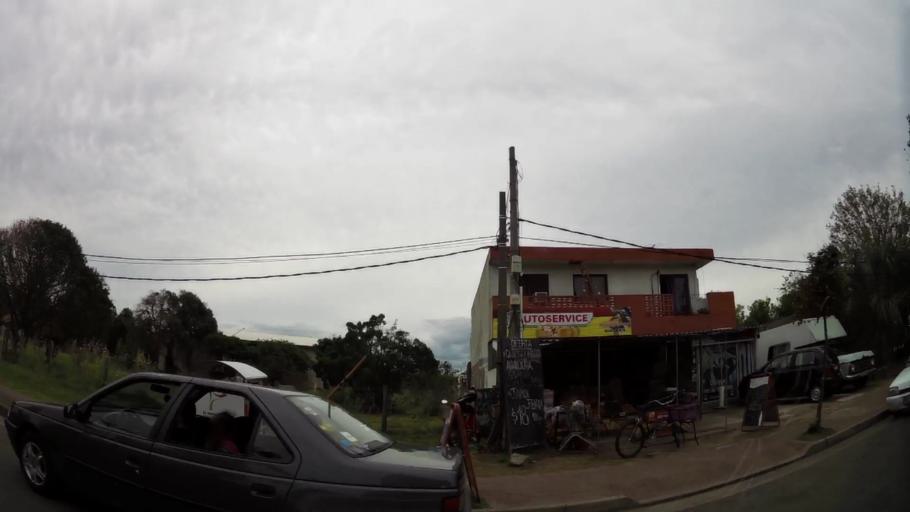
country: UY
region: Maldonado
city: Maldonado
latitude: -34.9020
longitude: -54.9701
